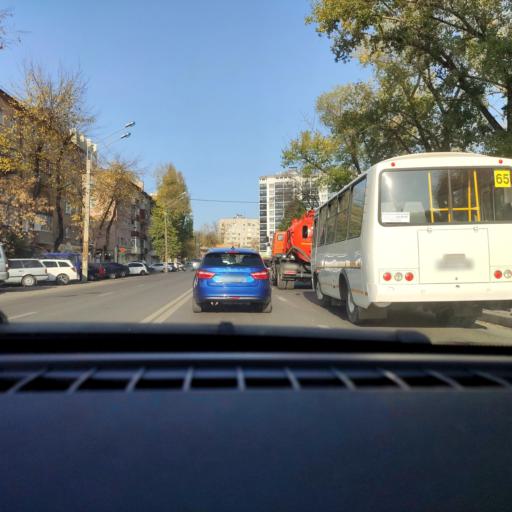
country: RU
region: Voronezj
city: Voronezh
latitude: 51.6597
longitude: 39.2768
